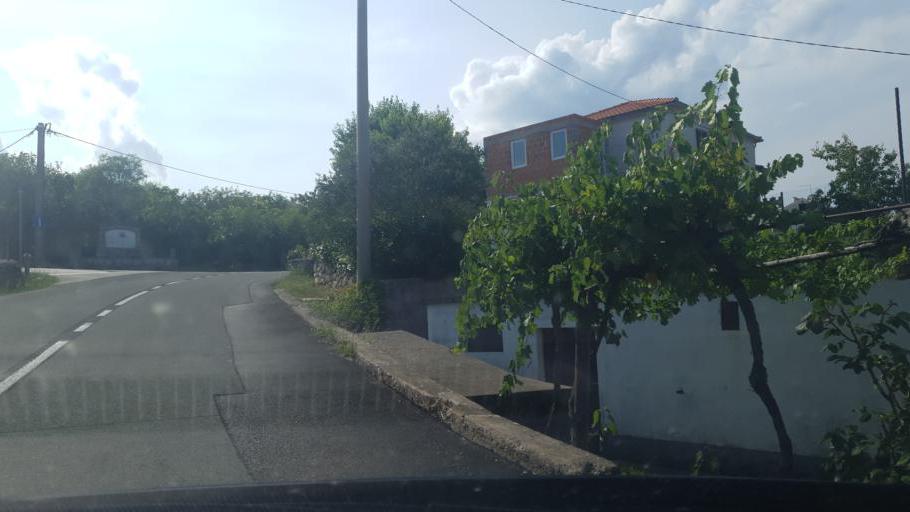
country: HR
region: Primorsko-Goranska
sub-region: Grad Crikvenica
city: Crikvenica
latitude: 45.1053
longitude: 14.6448
